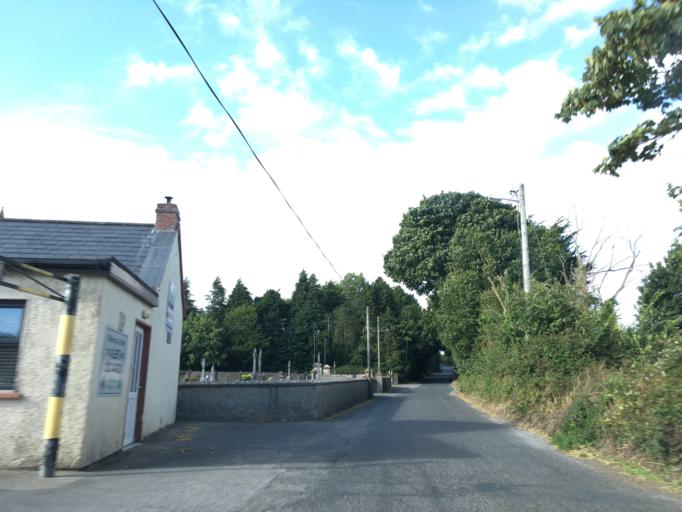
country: IE
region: Munster
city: Cahir
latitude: 52.2928
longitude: -7.9511
